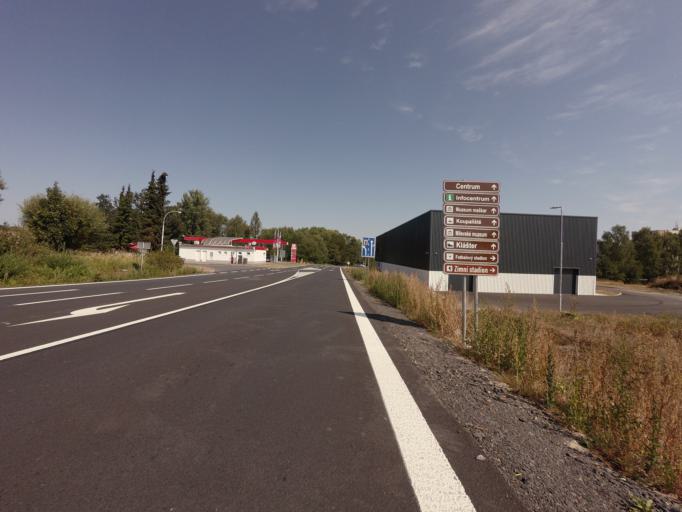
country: CZ
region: Jihocesky
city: Milevsko
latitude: 49.4406
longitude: 14.3589
